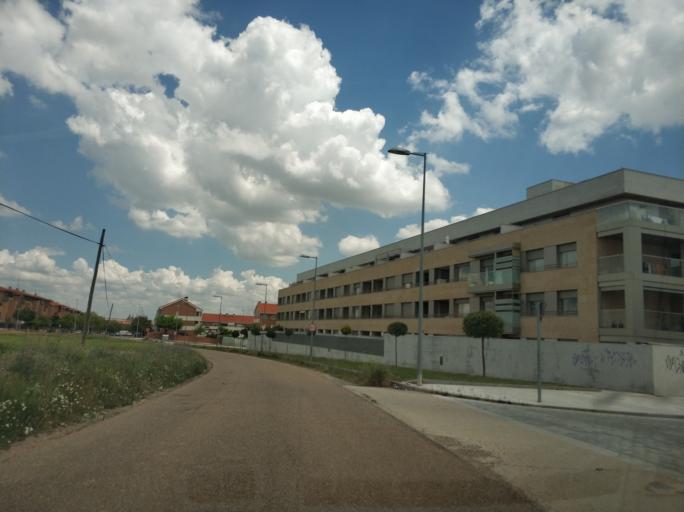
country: ES
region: Castille and Leon
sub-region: Provincia de Salamanca
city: Aldeatejada
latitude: 40.9467
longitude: -5.6843
